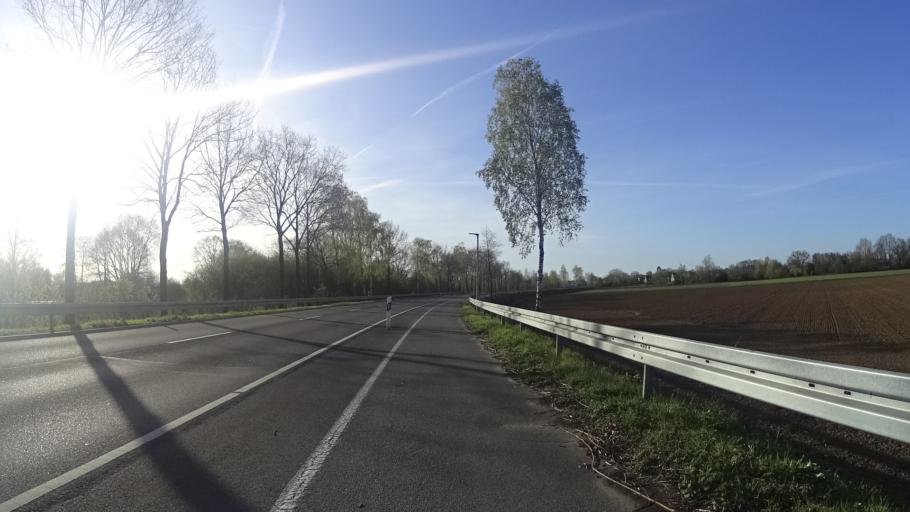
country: DE
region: North Rhine-Westphalia
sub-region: Regierungsbezirk Munster
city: Greven
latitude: 52.1105
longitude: 7.5814
